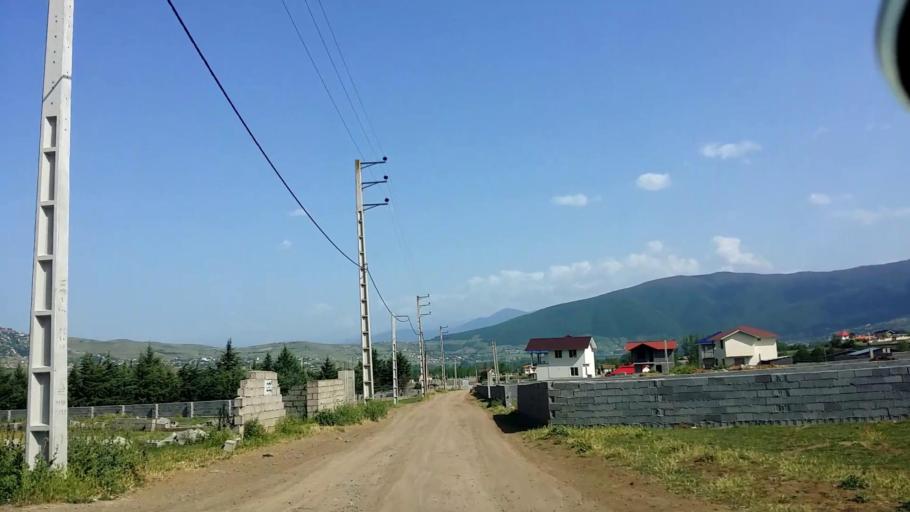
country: IR
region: Mazandaran
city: `Abbasabad
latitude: 36.5454
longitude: 51.1871
